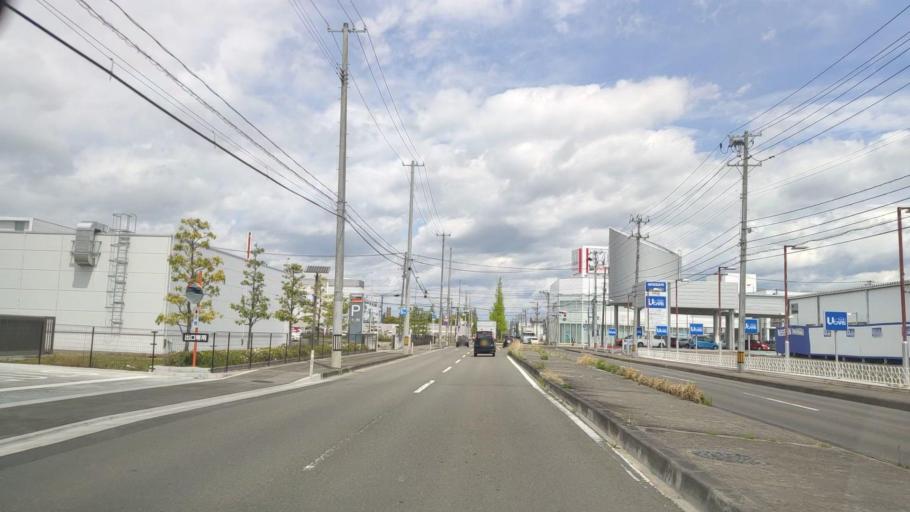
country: JP
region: Miyagi
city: Rifu
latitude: 38.2679
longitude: 140.9435
